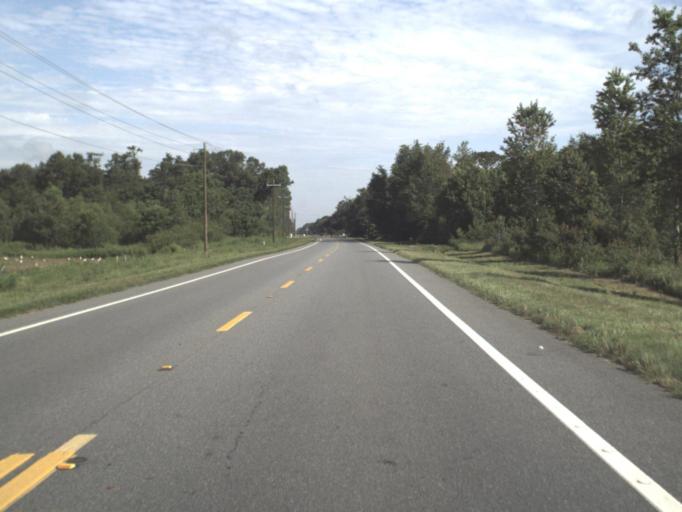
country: US
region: Florida
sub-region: Madison County
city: Madison
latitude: 30.4068
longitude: -83.3653
